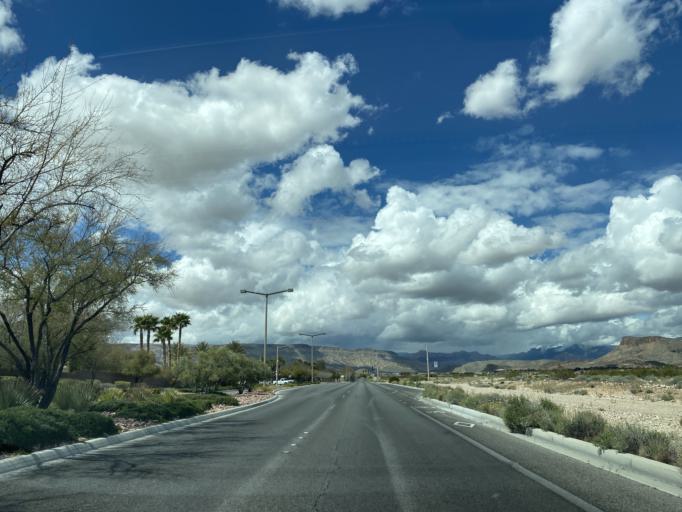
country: US
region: Nevada
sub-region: Clark County
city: Summerlin South
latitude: 36.1154
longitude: -115.3210
